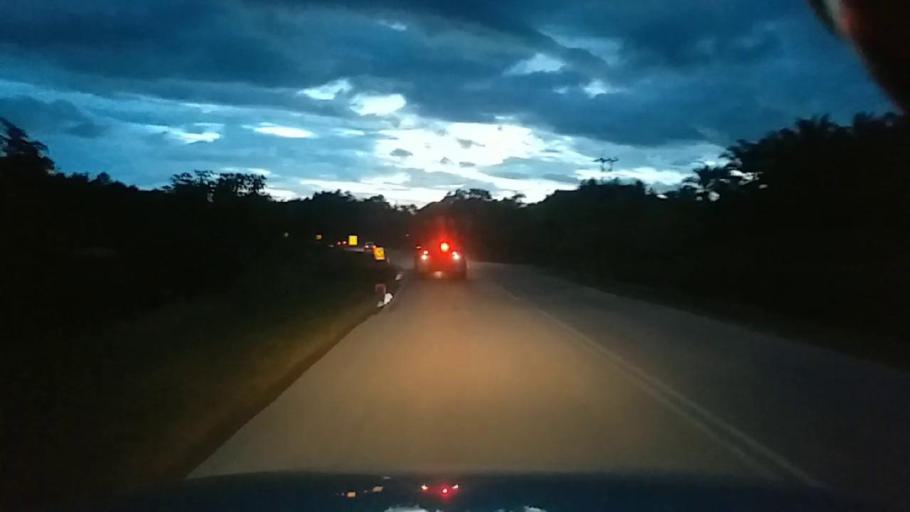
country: MY
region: Sarawak
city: Sibu
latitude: 2.4165
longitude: 112.1689
